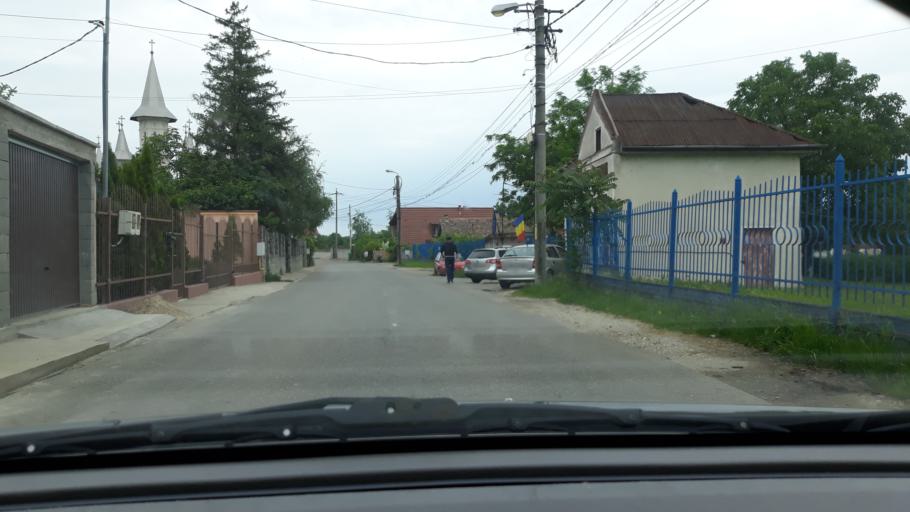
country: RO
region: Bihor
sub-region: Comuna Biharea
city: Oradea
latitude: 47.0522
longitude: 21.9644
